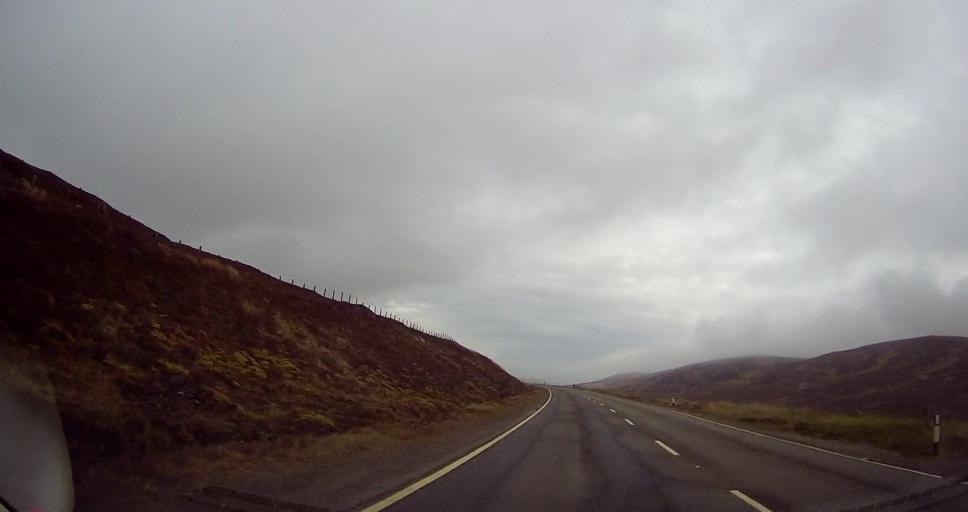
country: GB
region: Scotland
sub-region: Shetland Islands
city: Lerwick
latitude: 60.1456
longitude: -1.2415
